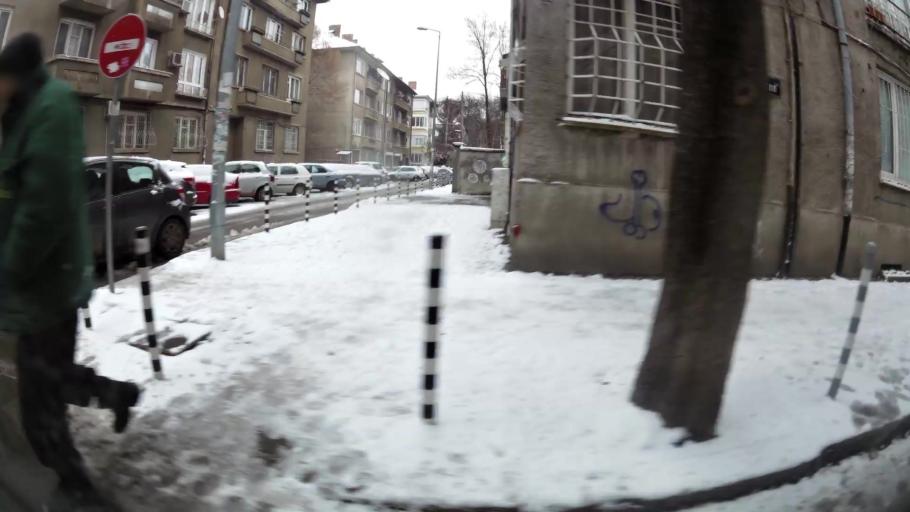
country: BG
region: Sofia-Capital
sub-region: Stolichna Obshtina
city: Sofia
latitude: 42.6909
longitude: 23.3422
